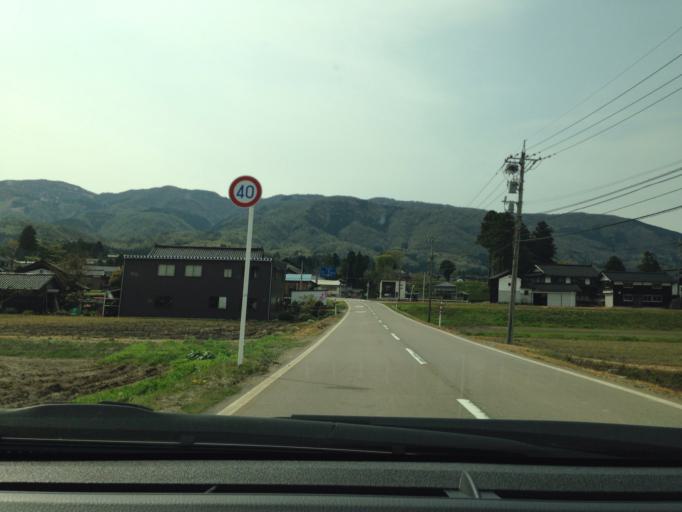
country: JP
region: Toyama
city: Fukumitsu
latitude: 36.5222
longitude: 136.8515
